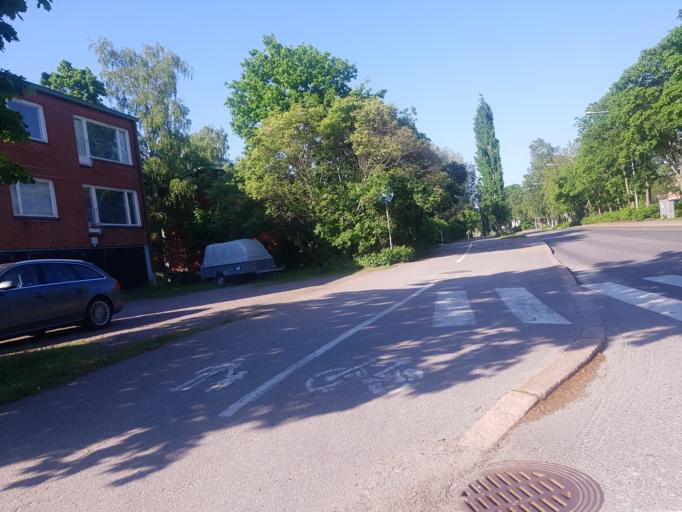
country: FI
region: Uusimaa
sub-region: Helsinki
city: Vantaa
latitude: 60.2542
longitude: 24.9941
